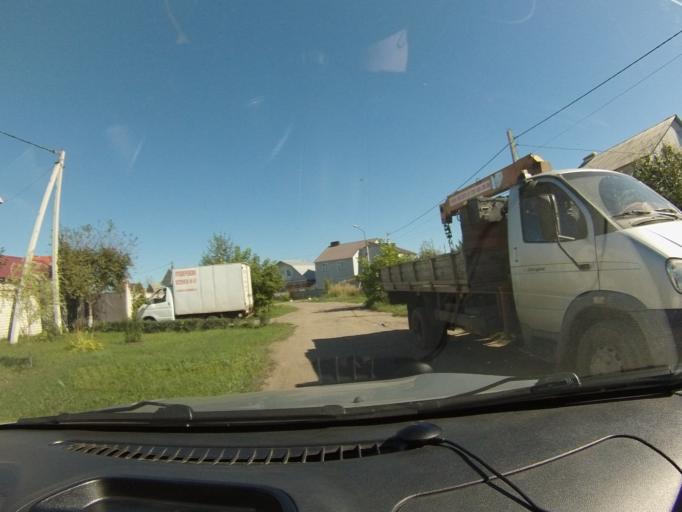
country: RU
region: Tambov
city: Tambov
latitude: 52.7600
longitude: 41.3702
